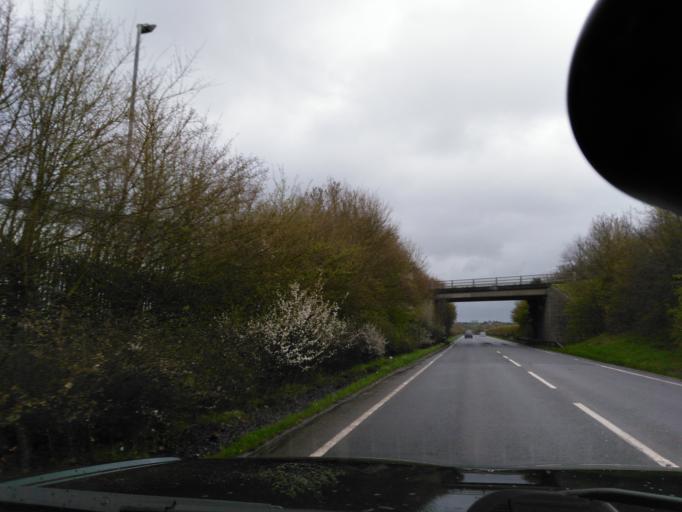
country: GB
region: England
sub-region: Somerset
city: Frome
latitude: 51.2458
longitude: -2.2898
